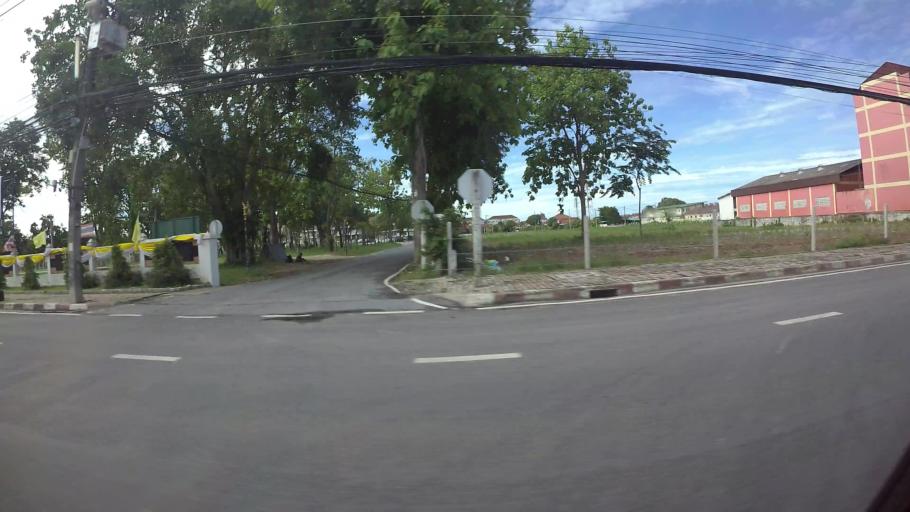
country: TH
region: Rayong
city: Ban Chang
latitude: 12.7295
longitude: 101.0650
